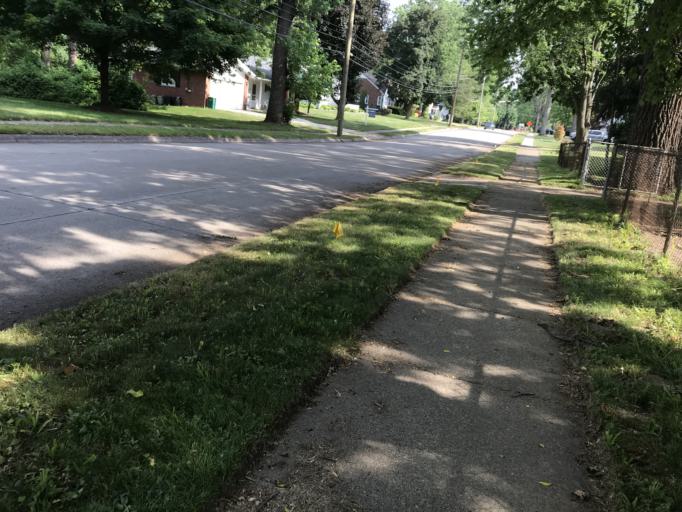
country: US
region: Michigan
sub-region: Oakland County
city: Farmington
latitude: 42.4587
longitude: -83.3688
